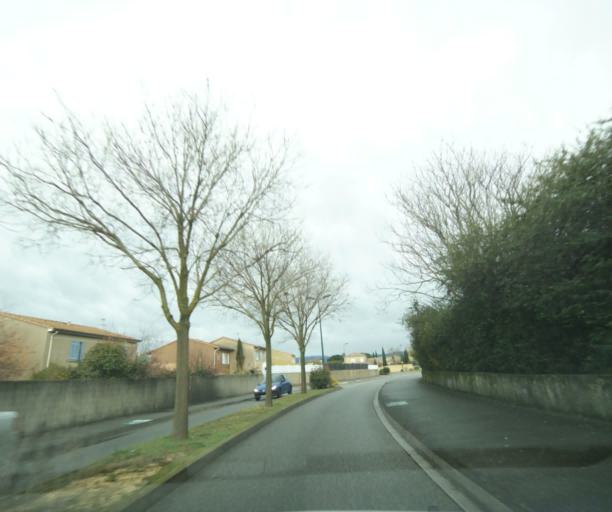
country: FR
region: Rhone-Alpes
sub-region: Departement de la Drome
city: Bourg-les-Valence
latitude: 44.9557
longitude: 4.9162
